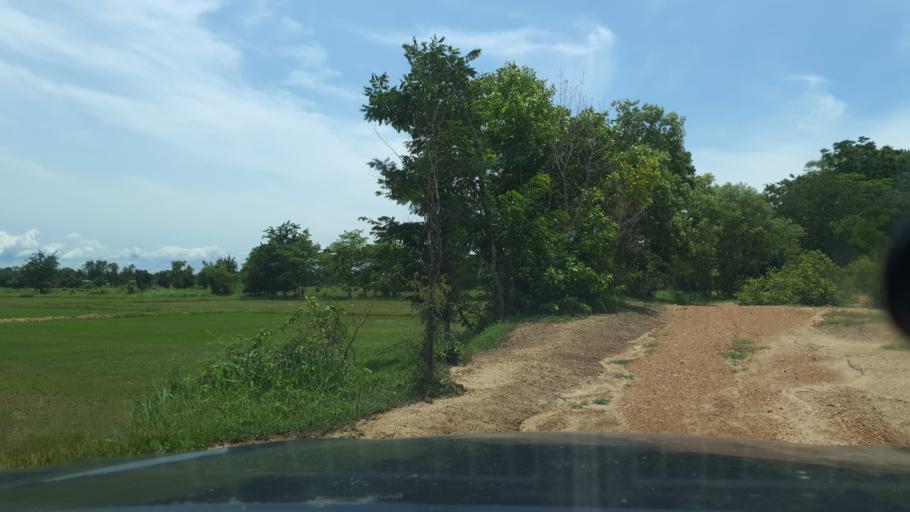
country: TH
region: Sukhothai
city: Ban Na
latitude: 17.0787
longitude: 99.6855
